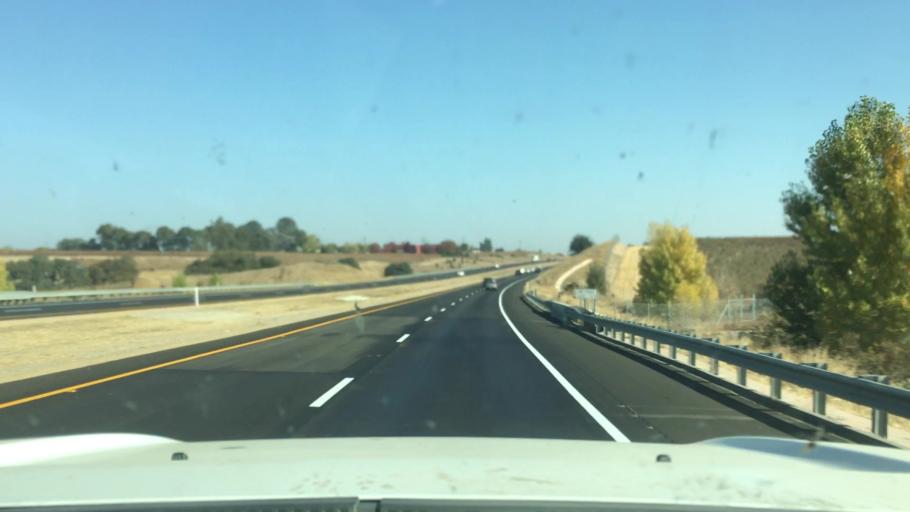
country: US
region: California
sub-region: San Luis Obispo County
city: Paso Robles
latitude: 35.6563
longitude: -120.6109
